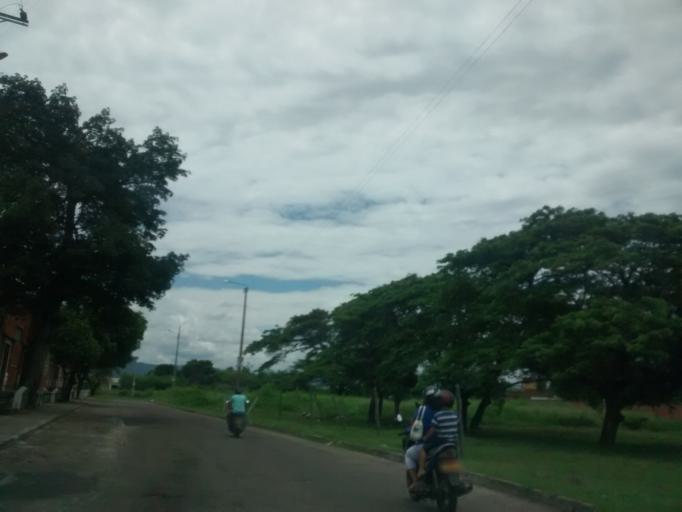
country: CO
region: Cundinamarca
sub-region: Girardot
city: Girardot City
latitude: 4.3045
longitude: -74.8055
